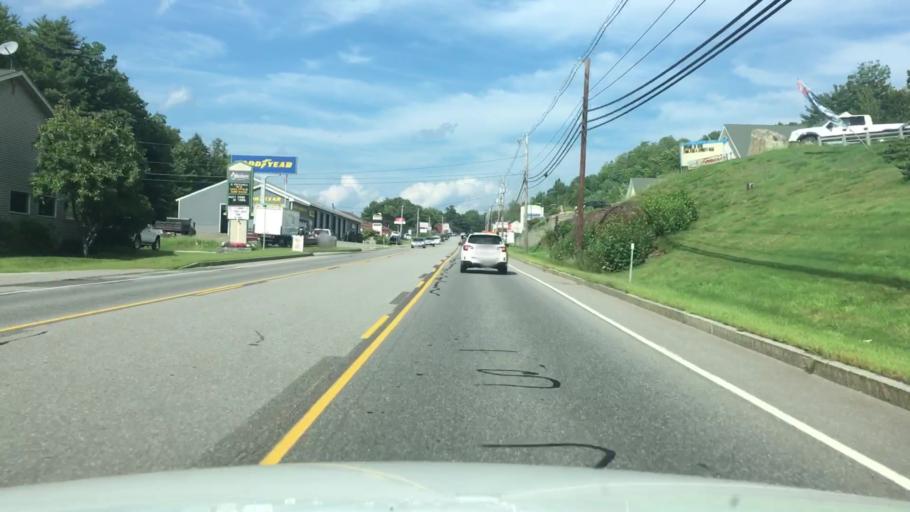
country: US
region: New Hampshire
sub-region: Belknap County
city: Laconia
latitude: 43.5100
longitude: -71.4983
